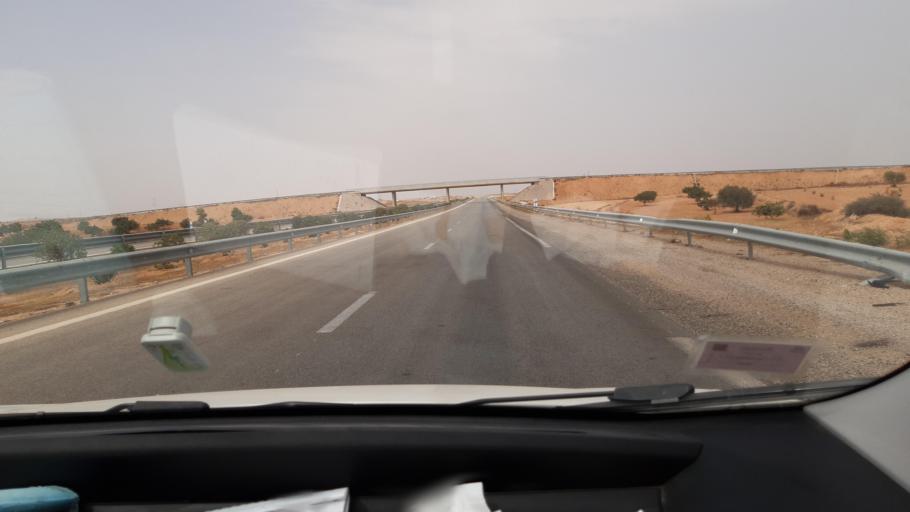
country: TN
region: Safaqis
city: Sfax
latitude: 34.7662
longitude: 10.6094
